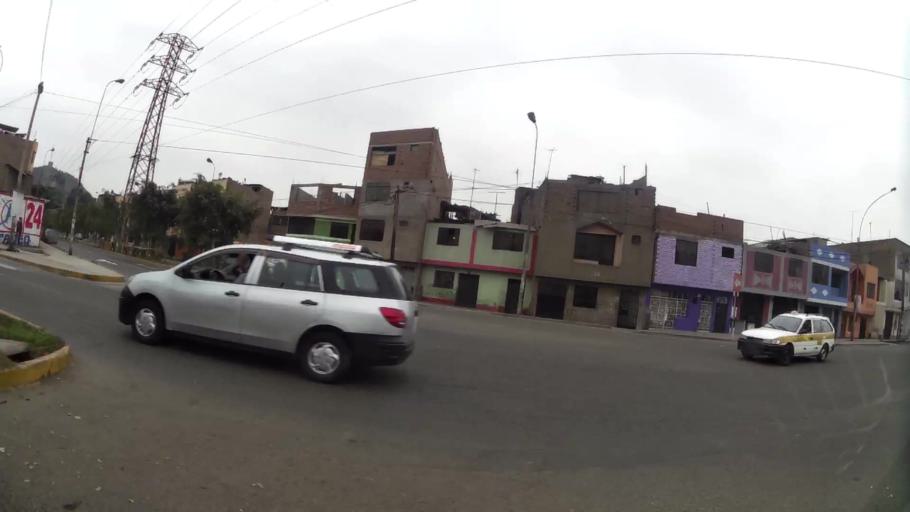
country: PE
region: Lima
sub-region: Lima
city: San Luis
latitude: -12.0411
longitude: -76.9755
